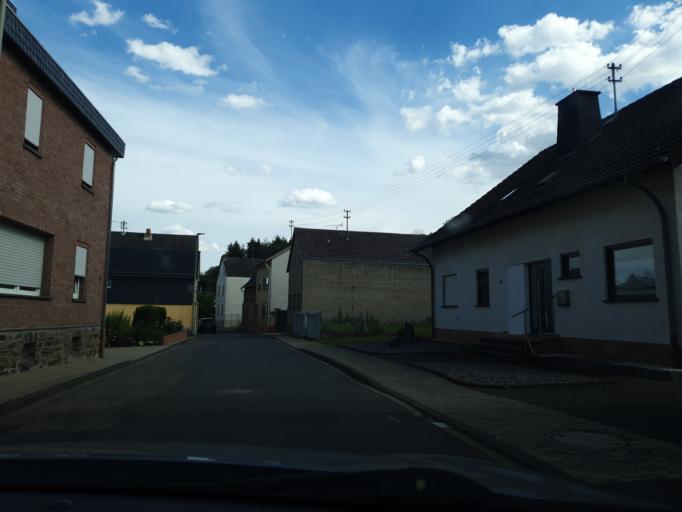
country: DE
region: Rheinland-Pfalz
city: Niederzissen
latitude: 50.4600
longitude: 7.2524
